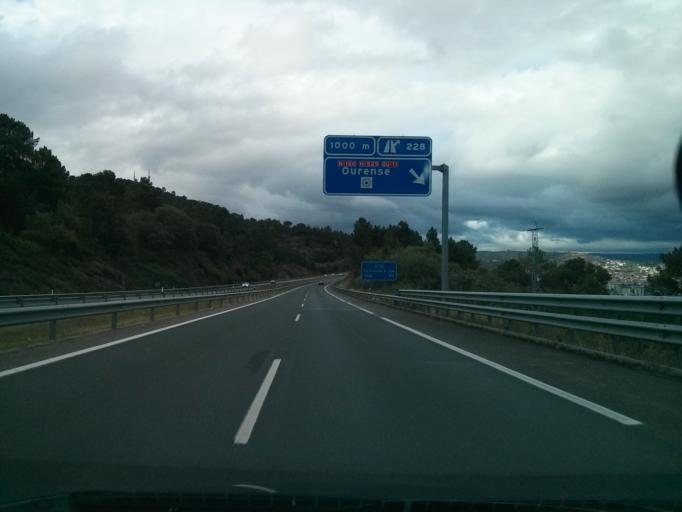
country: ES
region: Galicia
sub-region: Provincia de Ourense
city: Ourense
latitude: 42.3299
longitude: -7.8871
